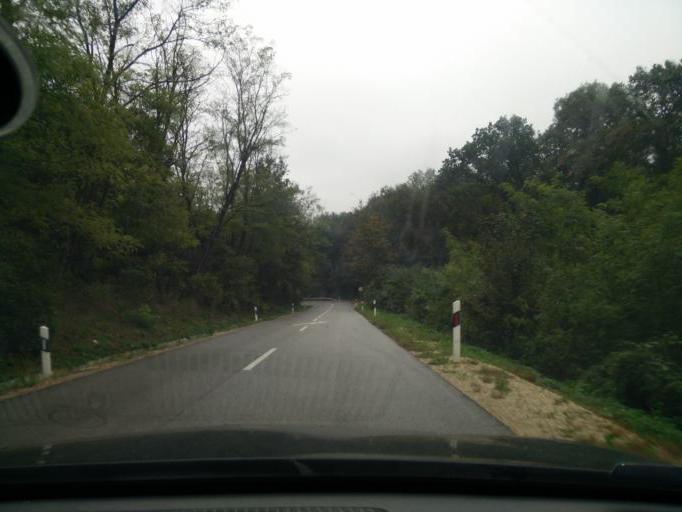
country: HU
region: Komarom-Esztergom
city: Bajna
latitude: 47.6354
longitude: 18.5641
